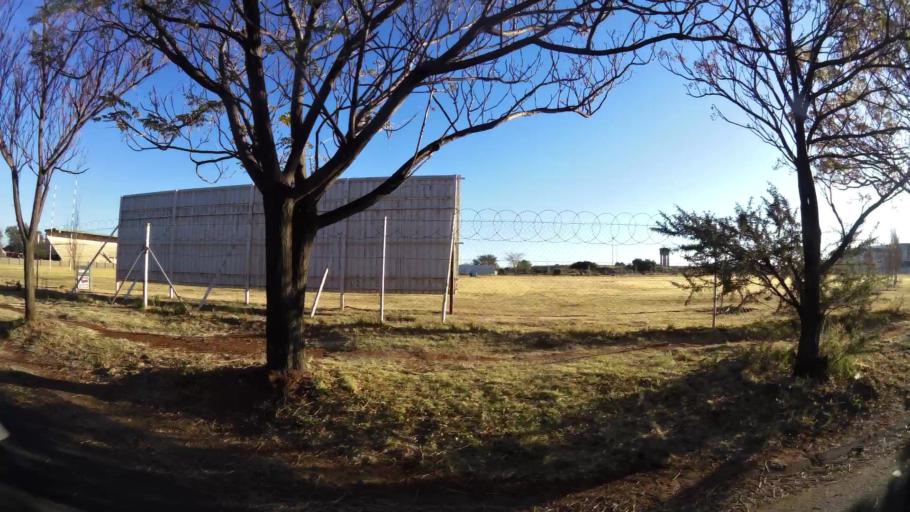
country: ZA
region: Northern Cape
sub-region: Frances Baard District Municipality
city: Kimberley
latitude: -28.7570
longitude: 24.7525
